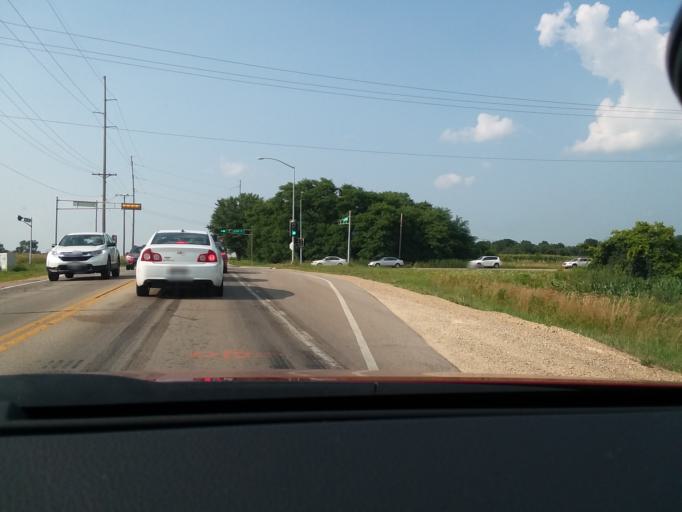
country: US
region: Wisconsin
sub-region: Dane County
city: Cottage Grove
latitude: 43.1062
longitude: -89.2667
